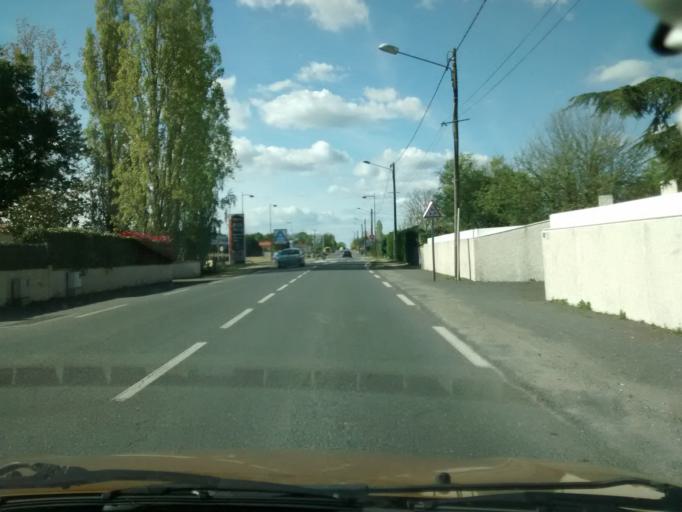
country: FR
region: Pays de la Loire
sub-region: Departement de la Loire-Atlantique
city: Geneston
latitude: 47.0618
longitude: -1.5158
